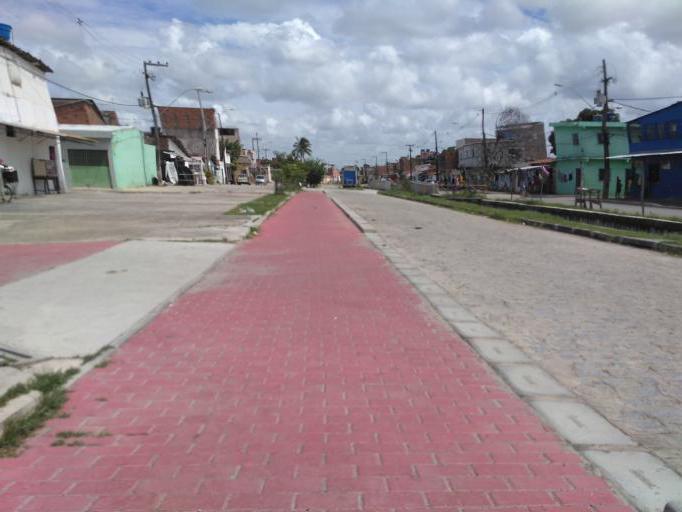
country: BR
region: Pernambuco
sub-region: Recife
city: Recife
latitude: -8.0725
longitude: -34.8972
